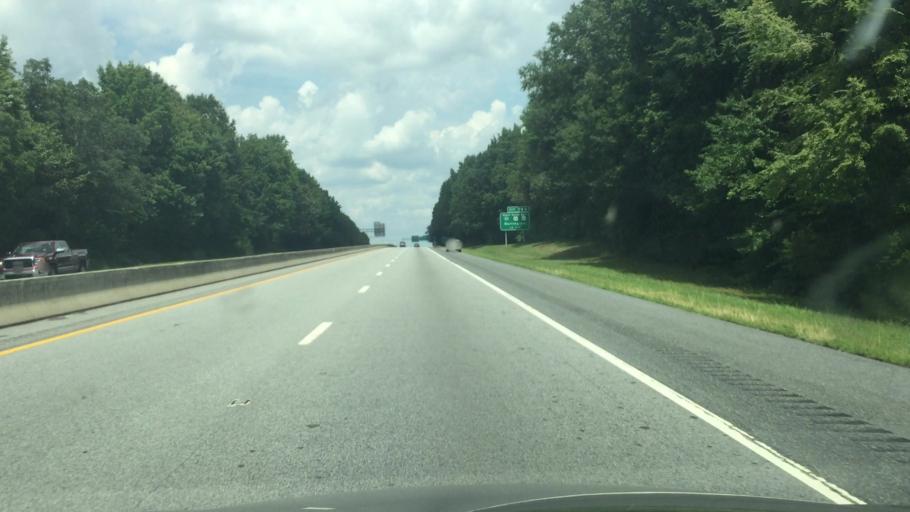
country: US
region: North Carolina
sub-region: Guilford County
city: Greensboro
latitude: 36.0114
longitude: -79.8263
